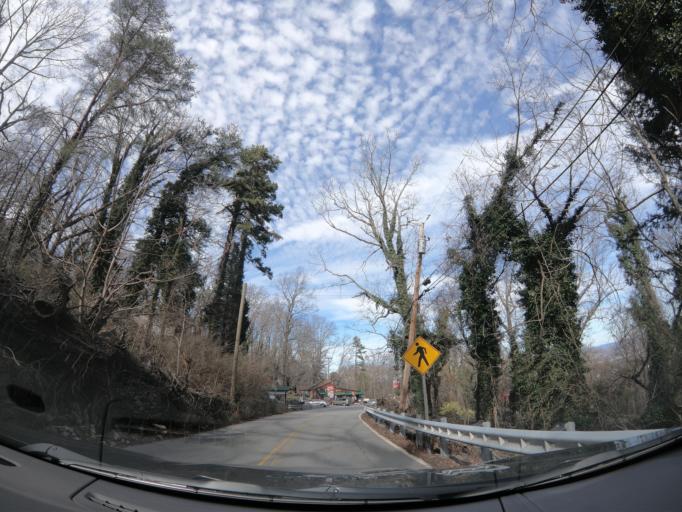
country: US
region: Tennessee
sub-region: Hamilton County
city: Lookout Mountain
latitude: 35.0064
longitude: -85.3385
